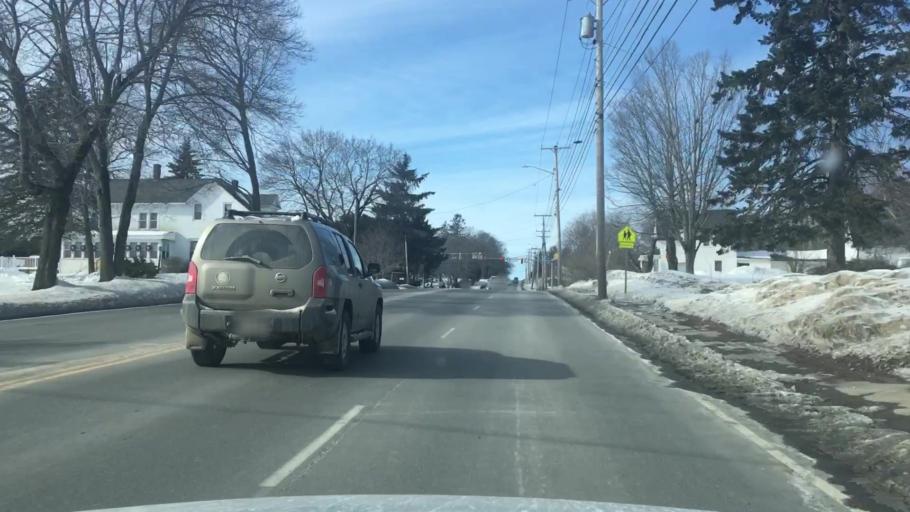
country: US
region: Maine
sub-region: Penobscot County
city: Bangor
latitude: 44.8263
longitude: -68.7820
